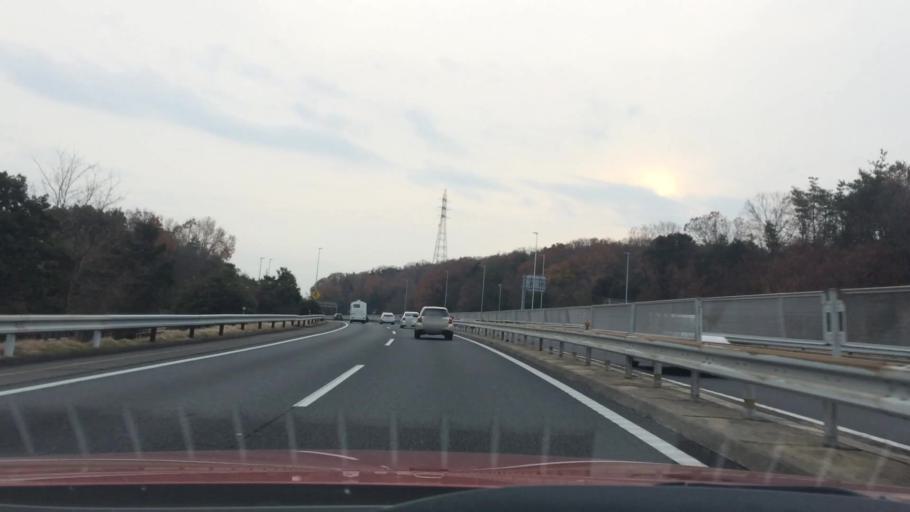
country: JP
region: Aichi
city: Kasugai
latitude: 35.3287
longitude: 137.0255
